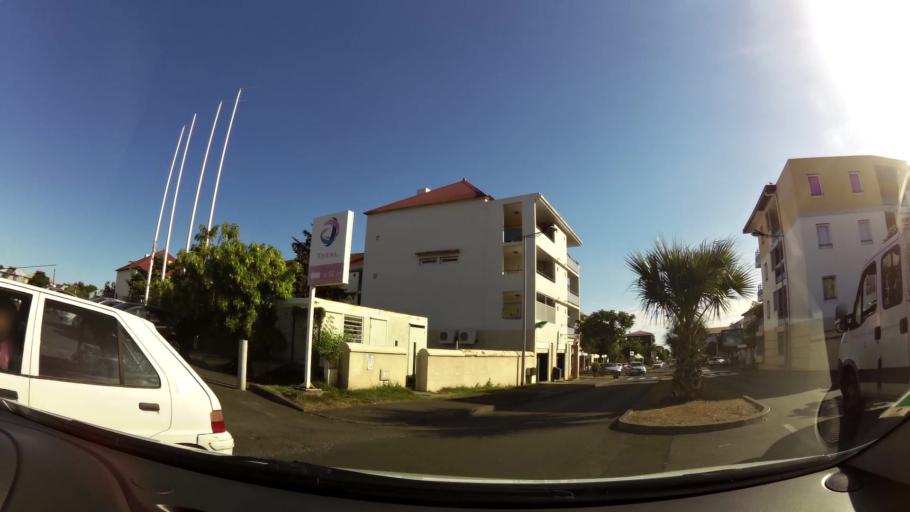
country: RE
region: Reunion
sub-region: Reunion
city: Saint-Louis
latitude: -21.2858
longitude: 55.4188
